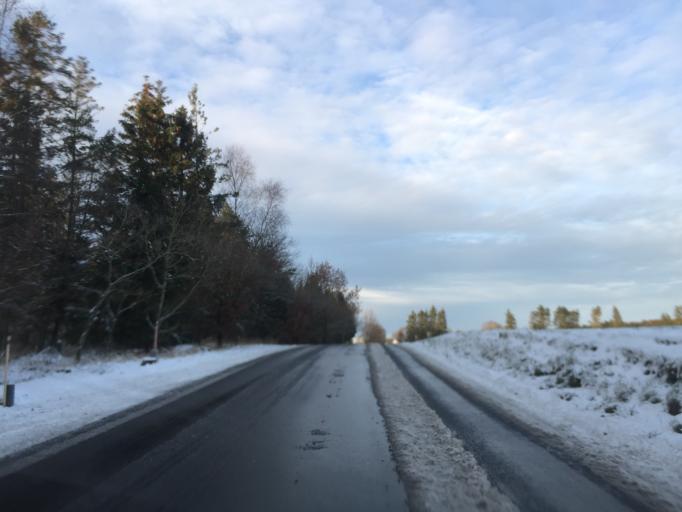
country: DK
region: Central Jutland
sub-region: Silkeborg Kommune
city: Svejbaek
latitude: 56.2190
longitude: 9.6825
